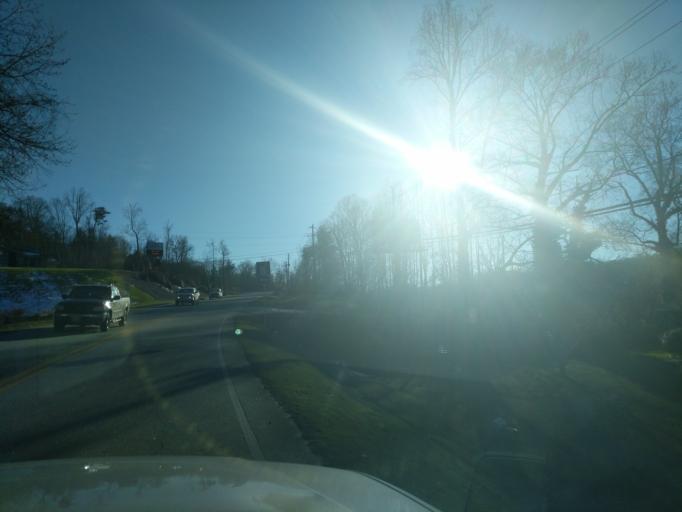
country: US
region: Georgia
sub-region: Rabun County
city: Clayton
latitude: 34.8735
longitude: -83.3984
